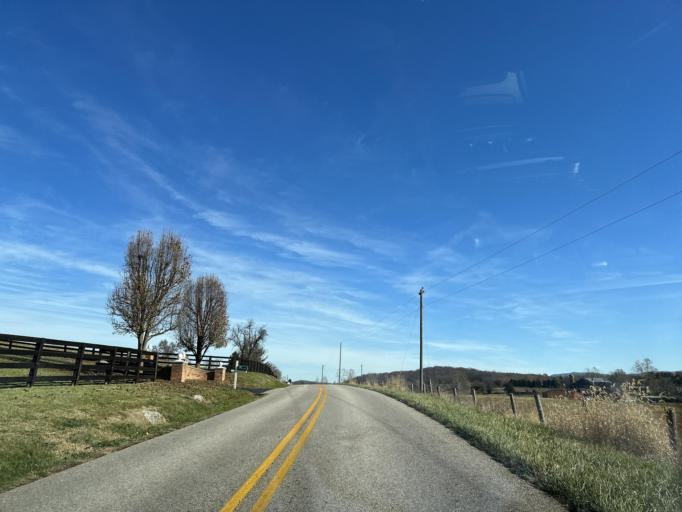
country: US
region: Virginia
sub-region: Augusta County
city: Fishersville
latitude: 38.1366
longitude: -78.9409
